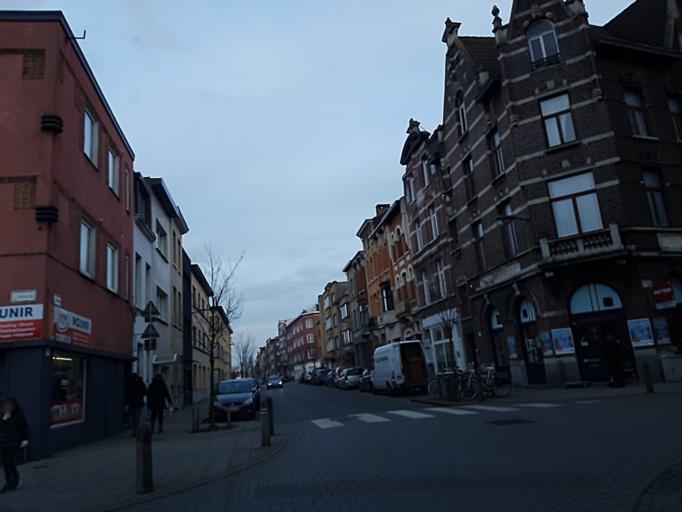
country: BE
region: Flanders
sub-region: Provincie Antwerpen
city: Antwerpen
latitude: 51.2112
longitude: 4.4341
